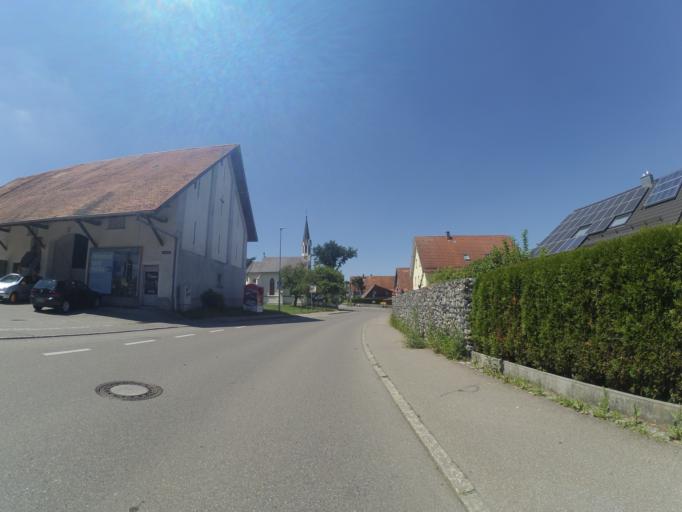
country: DE
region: Baden-Wuerttemberg
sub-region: Tuebingen Region
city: Bad Waldsee
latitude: 47.9202
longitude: 9.7368
